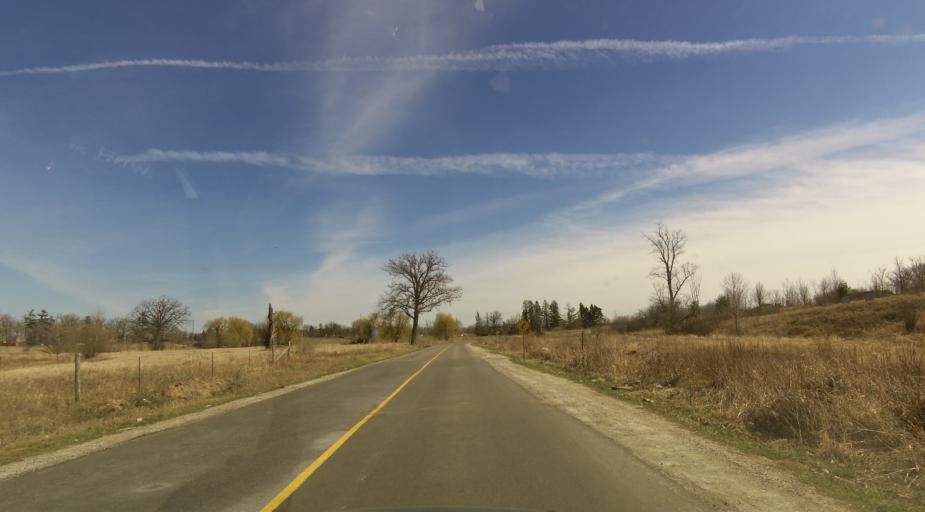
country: CA
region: Ontario
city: Brampton
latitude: 43.6397
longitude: -79.7688
